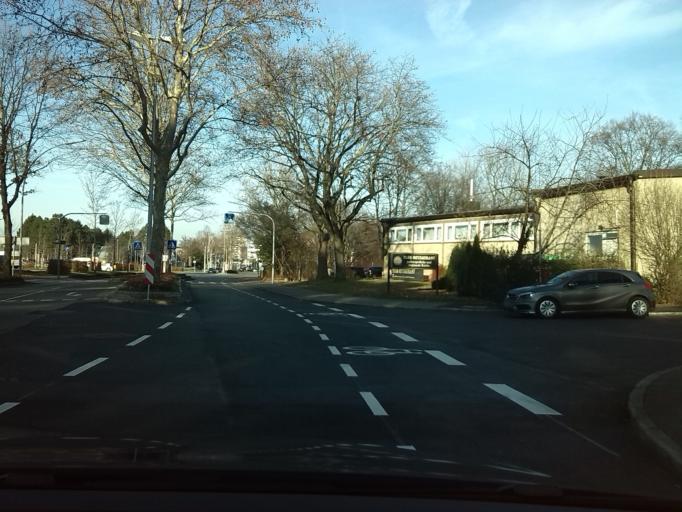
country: DE
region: Baden-Wuerttemberg
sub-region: Regierungsbezirk Stuttgart
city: Fellbach
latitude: 48.8069
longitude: 9.2697
